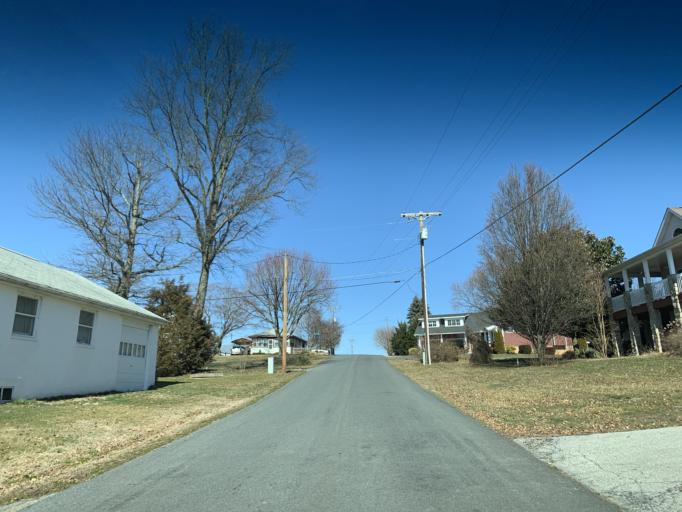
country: US
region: Maryland
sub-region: Cecil County
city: Charlestown
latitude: 39.4385
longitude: -75.9753
